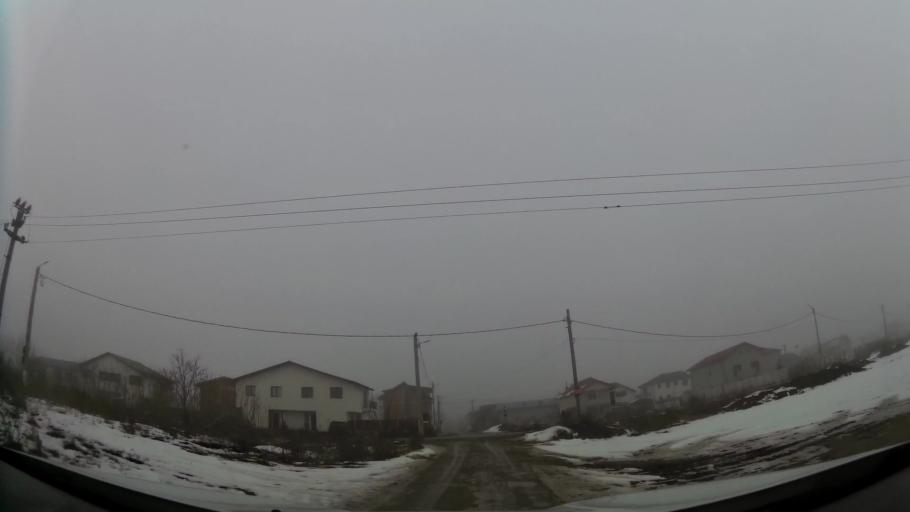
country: RO
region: Ilfov
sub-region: Comuna Chiajna
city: Chiajna
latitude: 44.4519
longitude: 25.9694
